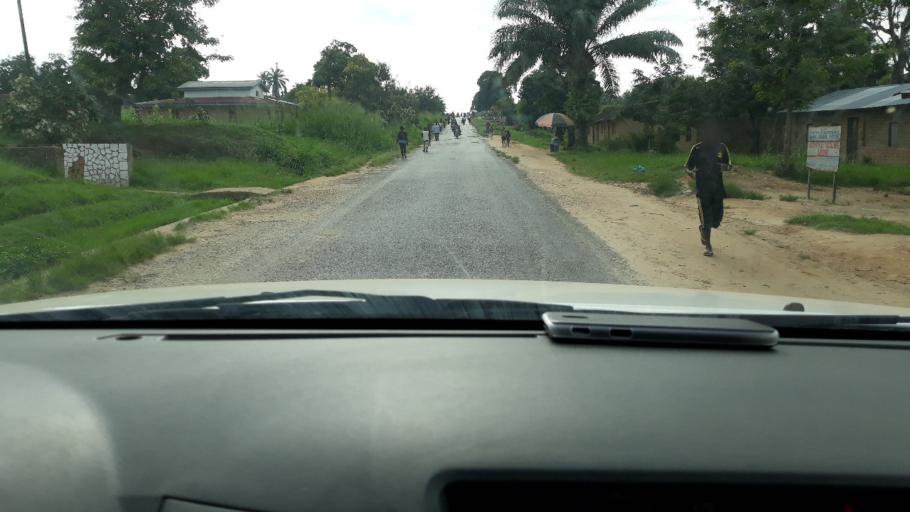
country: CD
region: Maniema
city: Kindu
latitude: -2.9517
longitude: 25.9445
